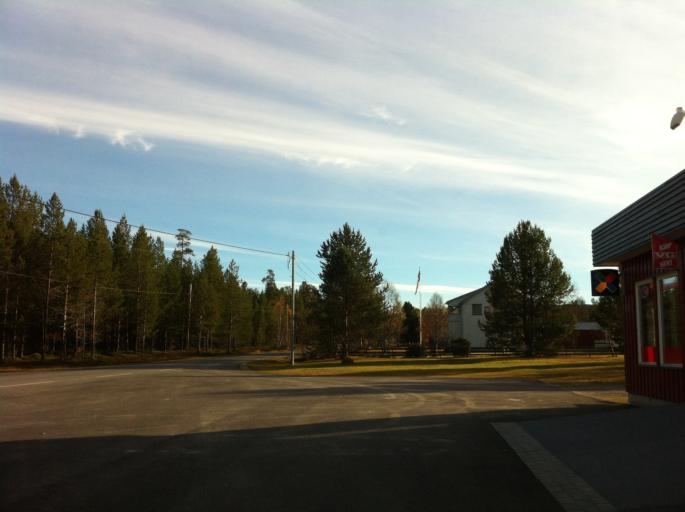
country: NO
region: Hedmark
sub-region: Engerdal
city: Engerdal
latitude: 62.1631
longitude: 11.9442
